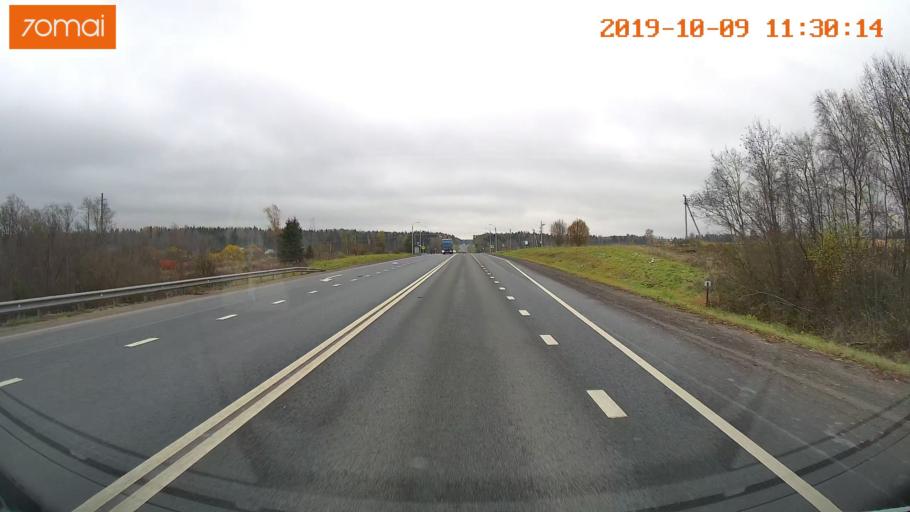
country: RU
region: Vologda
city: Vologda
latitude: 59.0555
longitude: 40.0706
